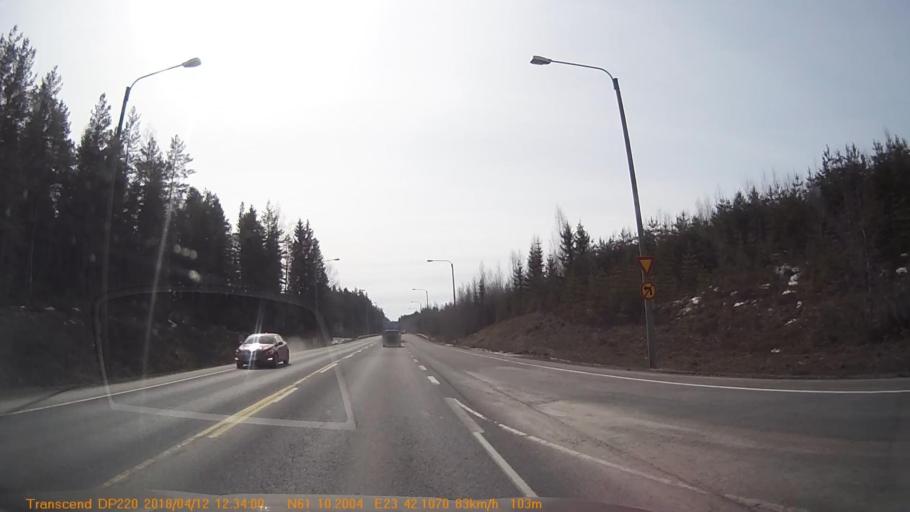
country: FI
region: Pirkanmaa
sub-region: Etelae-Pirkanmaa
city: Kylmaekoski
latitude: 61.1698
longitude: 23.7016
